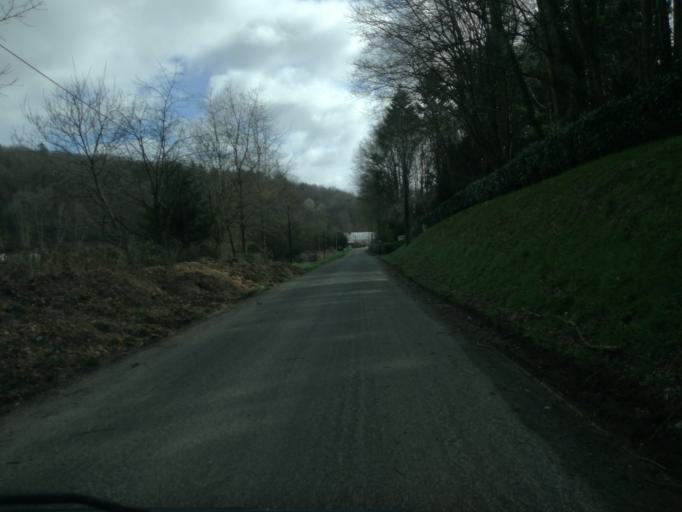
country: FR
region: Haute-Normandie
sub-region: Departement de la Seine-Maritime
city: Bretteville-du-Grand-Caux
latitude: 49.7004
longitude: 0.4557
